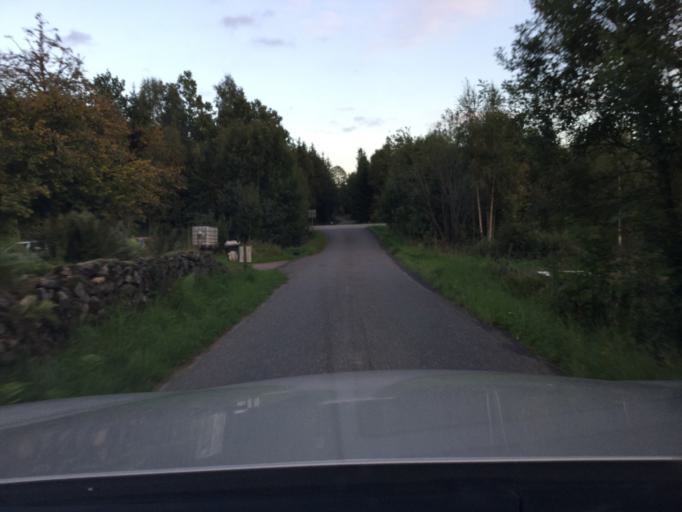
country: SE
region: Kronoberg
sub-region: Almhults Kommun
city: AElmhult
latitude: 56.6105
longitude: 14.2274
